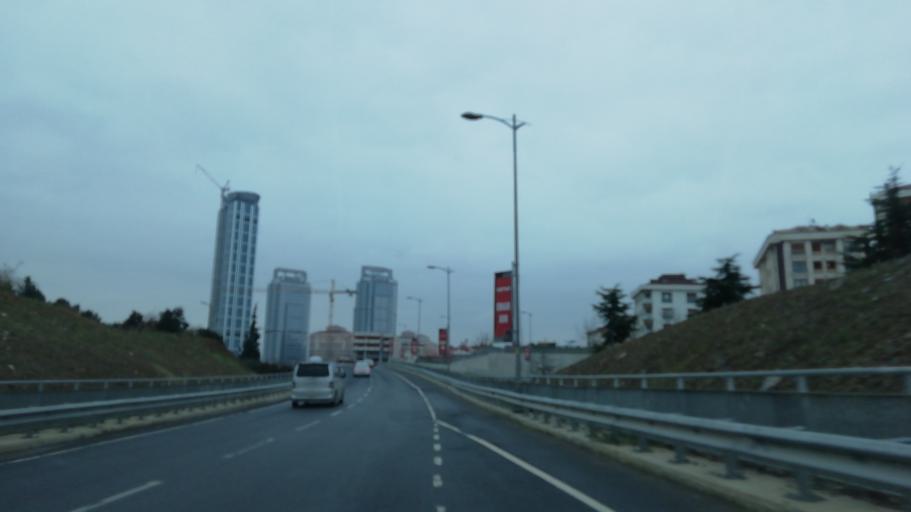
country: TR
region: Istanbul
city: UEskuedar
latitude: 41.0074
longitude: 29.0625
